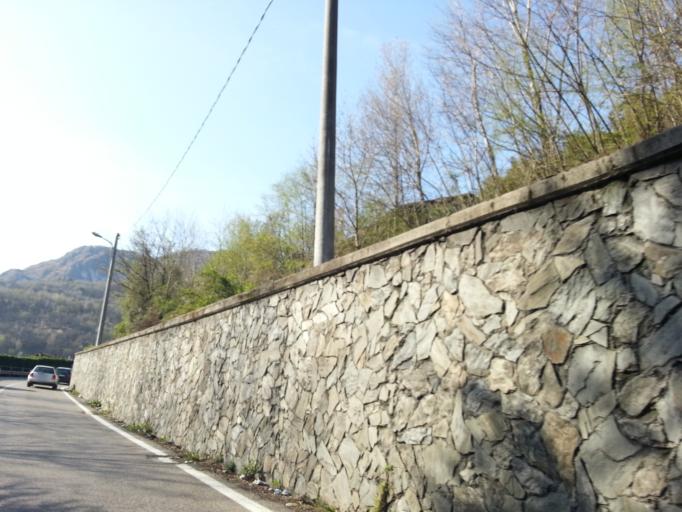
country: IT
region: Lombardy
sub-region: Provincia di Como
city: Menaggio
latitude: 46.0214
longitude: 9.2287
